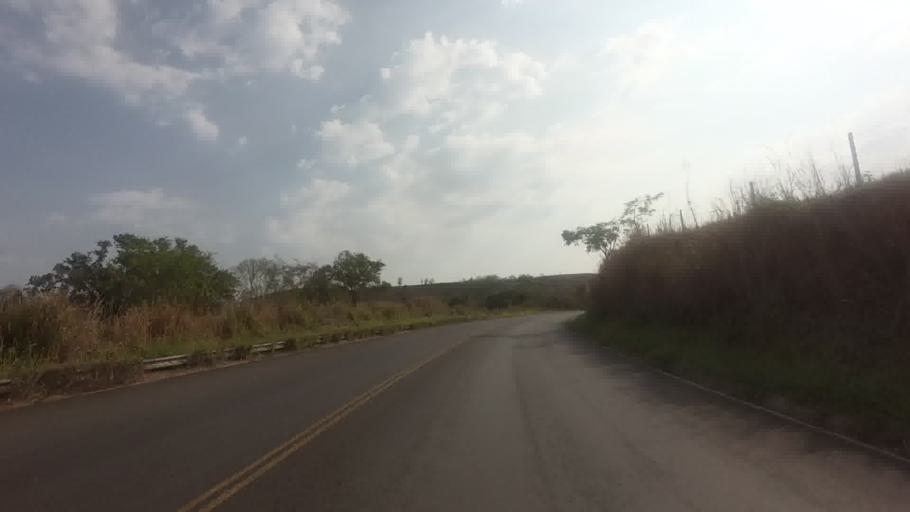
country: BR
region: Rio de Janeiro
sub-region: Itaperuna
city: Itaperuna
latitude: -21.3291
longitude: -41.8779
